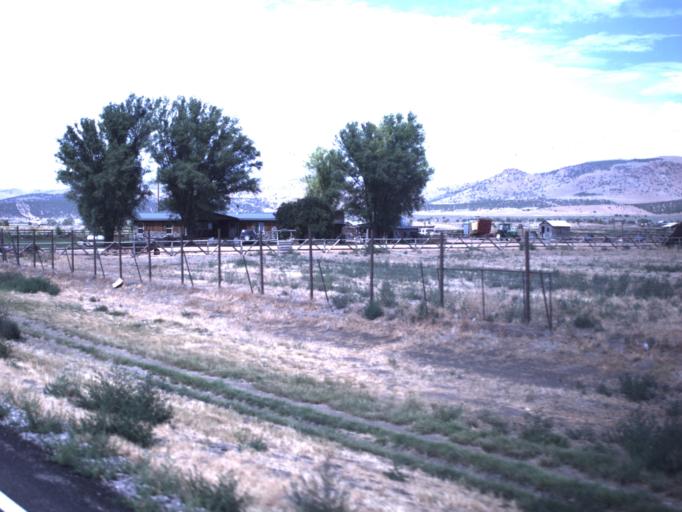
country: US
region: Utah
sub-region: Sanpete County
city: Fountain Green
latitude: 39.5984
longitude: -111.6207
